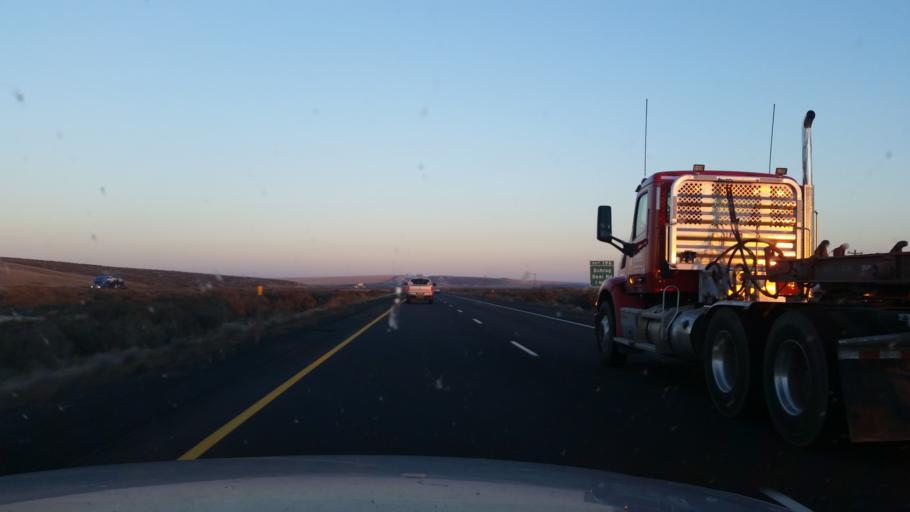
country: US
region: Washington
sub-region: Grant County
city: Warden
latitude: 47.0870
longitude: -118.9024
